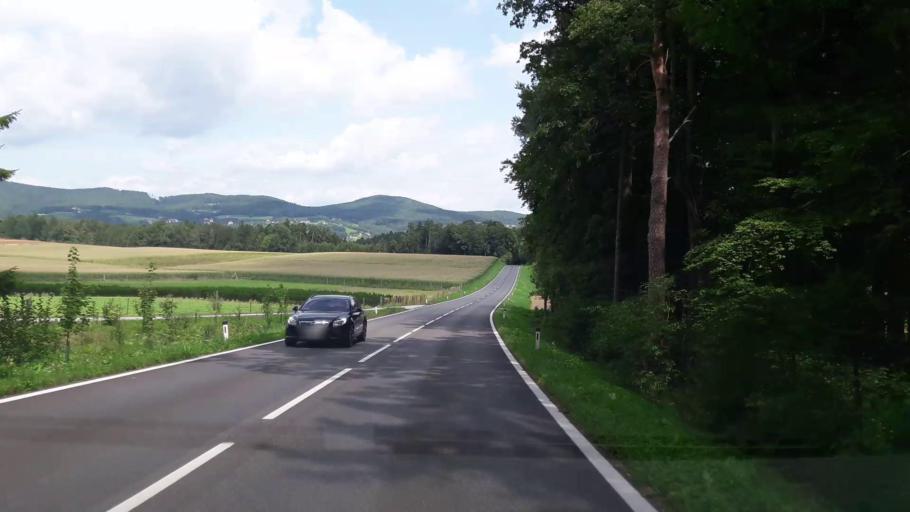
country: AT
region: Styria
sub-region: Politischer Bezirk Hartberg-Fuerstenfeld
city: Hartberg
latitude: 47.2548
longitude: 15.9368
